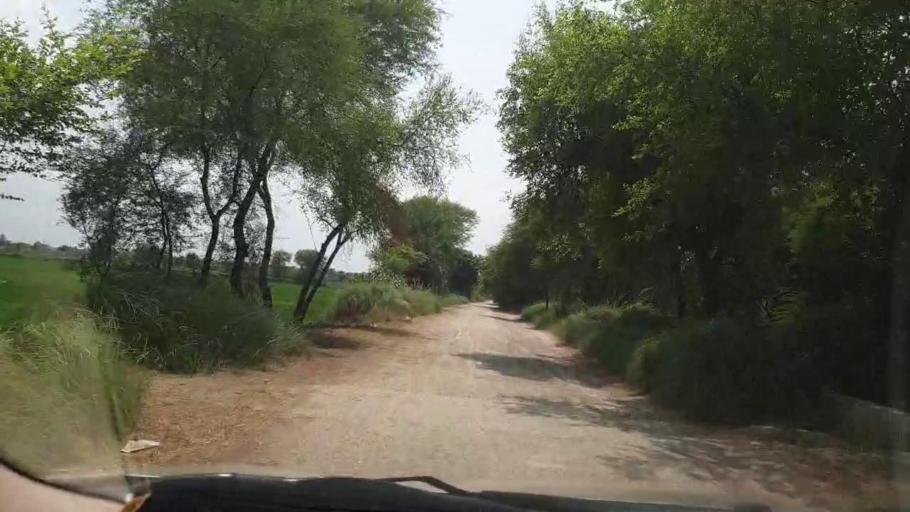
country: PK
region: Sindh
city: Larkana
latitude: 27.5857
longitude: 68.1177
